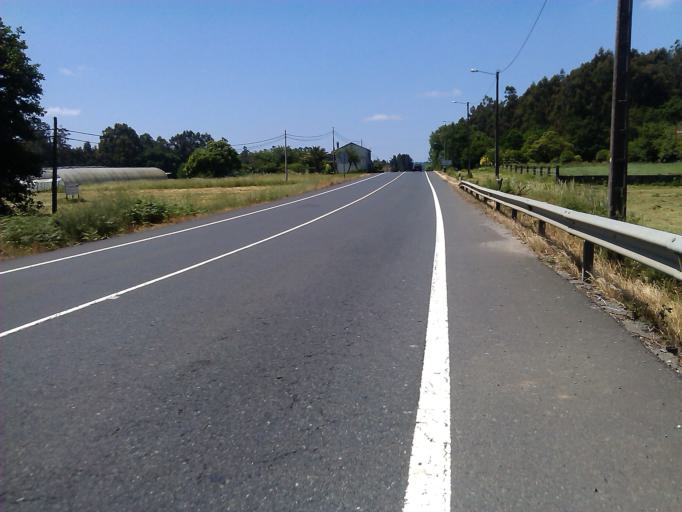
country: ES
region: Galicia
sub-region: Provincia da Coruna
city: Touro
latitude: 42.9037
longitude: -8.3716
